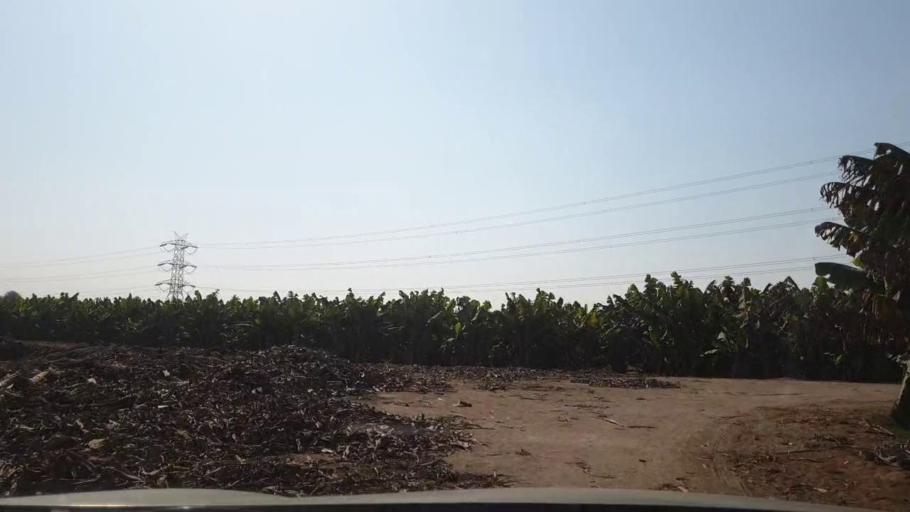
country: PK
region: Sindh
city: Tando Allahyar
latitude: 25.5026
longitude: 68.6920
